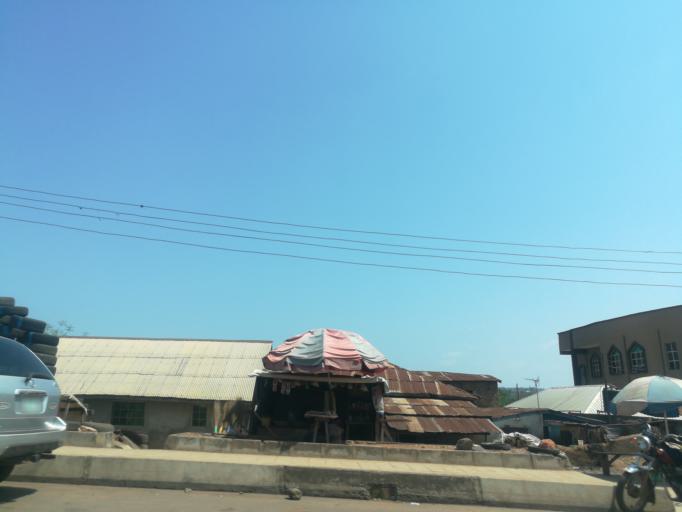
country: NG
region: Ogun
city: Abeokuta
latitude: 7.1682
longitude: 3.3583
